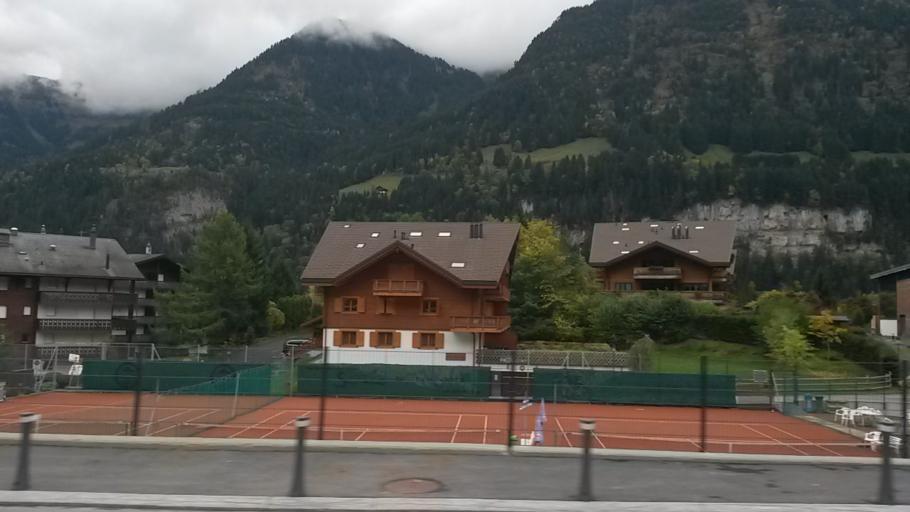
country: CH
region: Valais
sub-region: Monthey District
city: Champery
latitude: 46.1777
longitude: 6.8717
